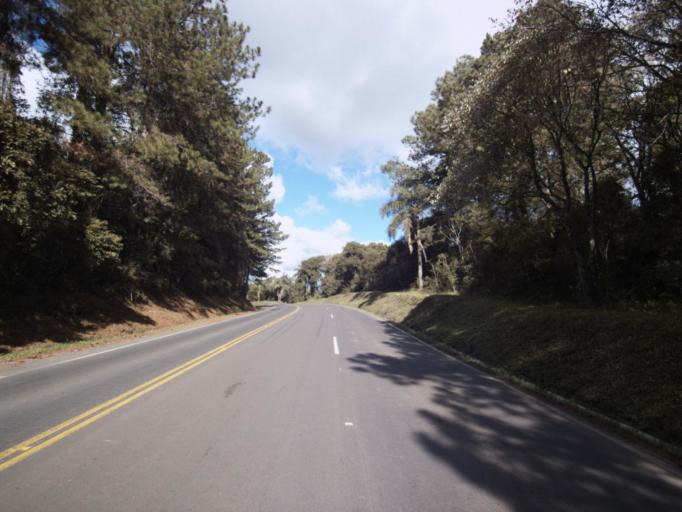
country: BR
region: Santa Catarina
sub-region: Joacaba
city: Joacaba
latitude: -27.0236
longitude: -51.7328
